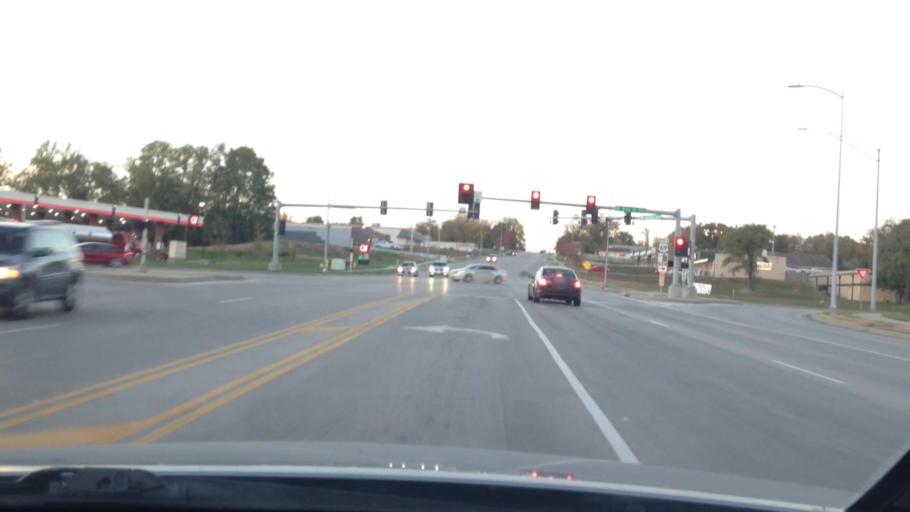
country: US
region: Missouri
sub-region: Platte County
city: Riverside
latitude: 39.1770
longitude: -94.6133
